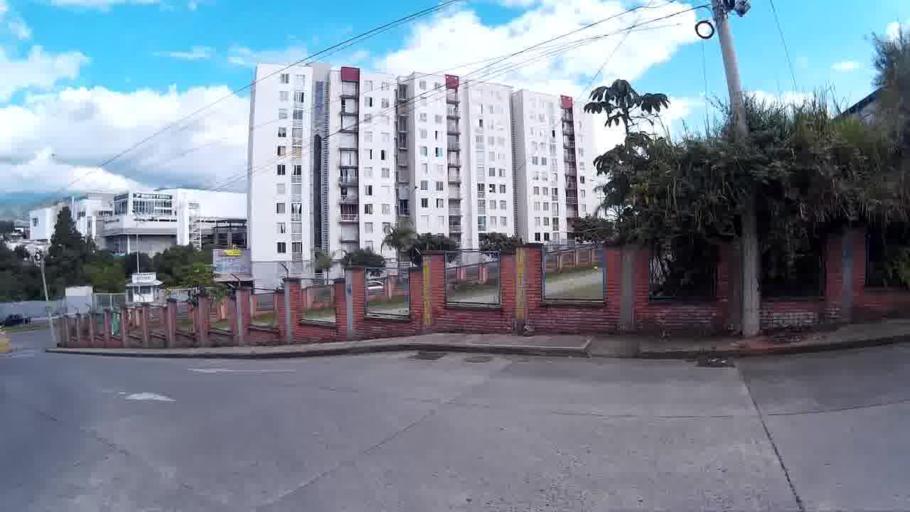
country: CO
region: Quindio
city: Armenia
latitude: 4.5429
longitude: -75.6620
